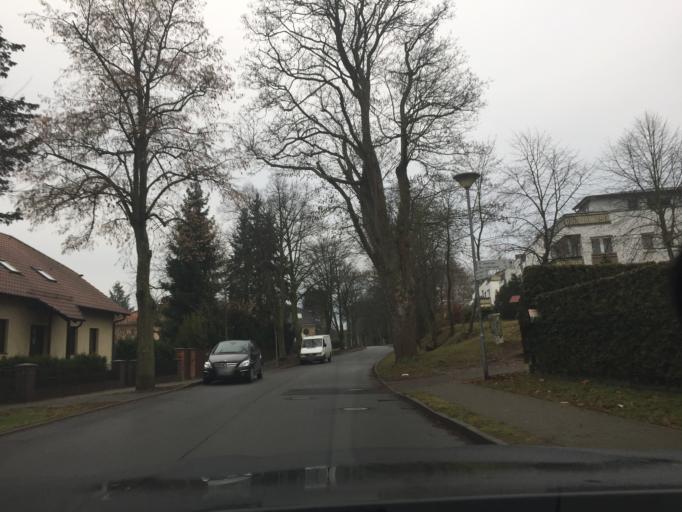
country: DE
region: Berlin
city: Kladow
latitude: 52.4689
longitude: 13.1085
